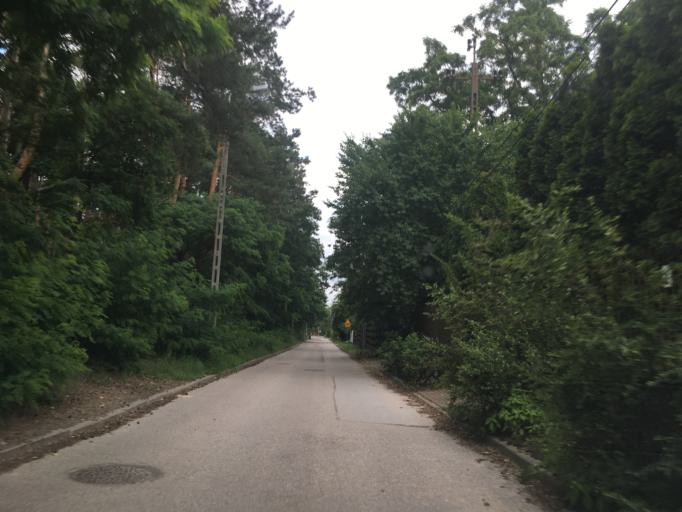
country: PL
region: Masovian Voivodeship
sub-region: Powiat piaseczynski
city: Lesznowola
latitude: 52.0762
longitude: 20.9507
